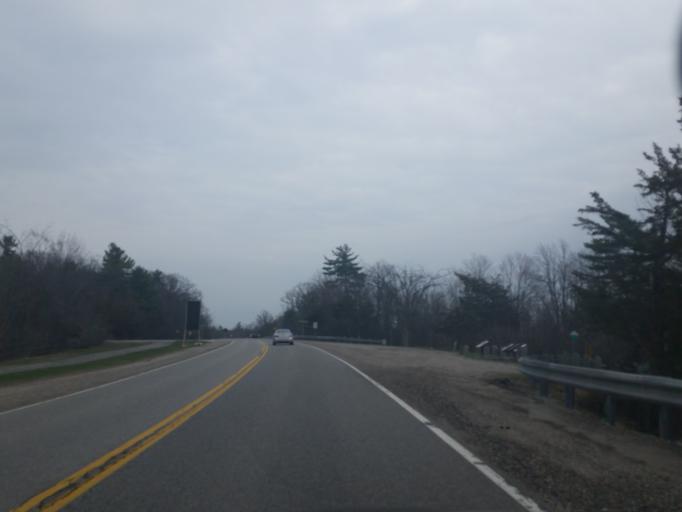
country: US
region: New York
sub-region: Jefferson County
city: Alexandria Bay
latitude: 44.3684
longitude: -75.9698
